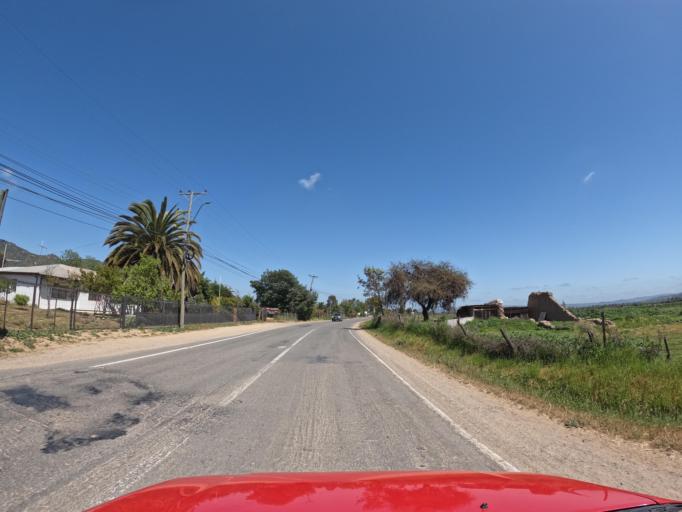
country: CL
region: O'Higgins
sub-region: Provincia de Colchagua
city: Santa Cruz
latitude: -34.7291
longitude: -71.6684
